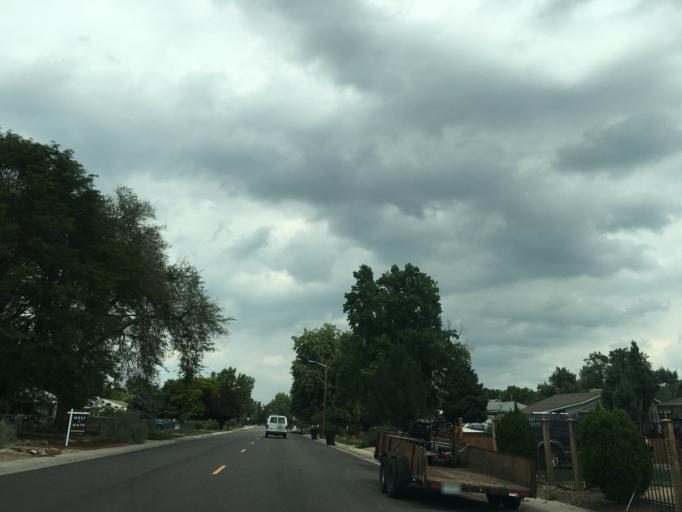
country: US
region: Colorado
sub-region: Arapahoe County
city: Sheridan
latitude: 39.6760
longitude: -105.0298
